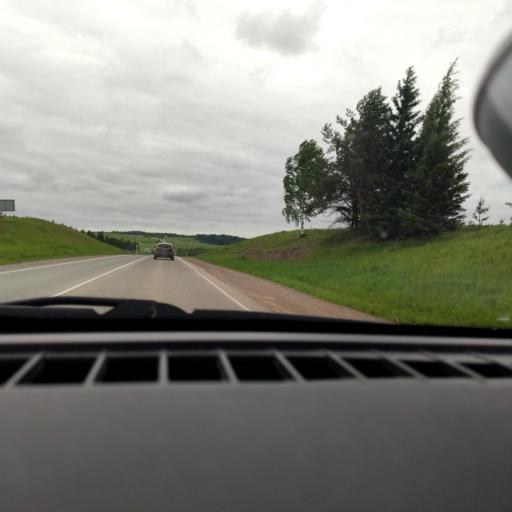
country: RU
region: Perm
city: Ust'-Kachka
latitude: 57.9034
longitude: 55.7813
